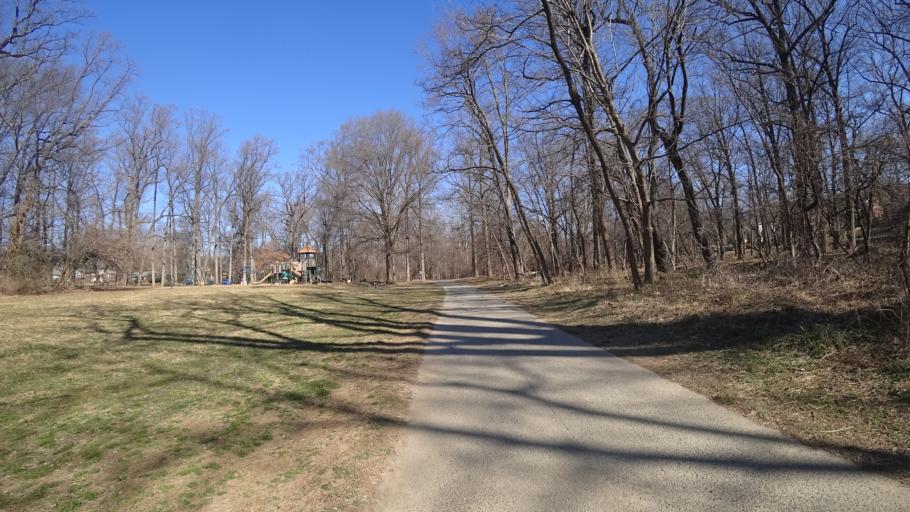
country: US
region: Maryland
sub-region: Montgomery County
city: Four Corners
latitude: 39.0174
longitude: -77.0332
